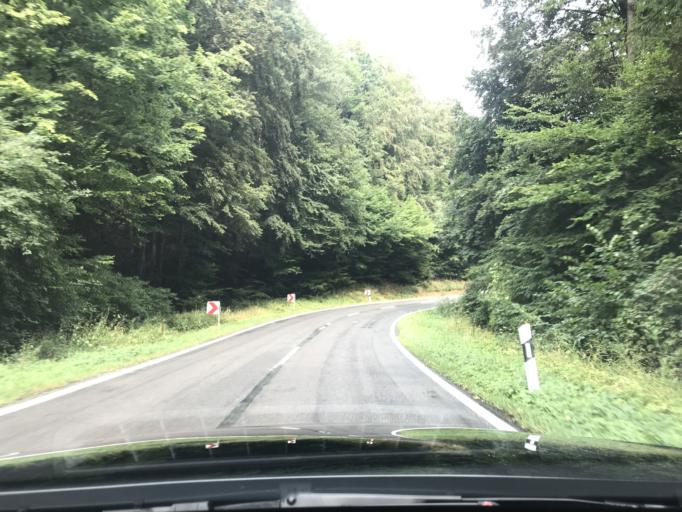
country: DE
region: Bavaria
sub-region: Regierungsbezirk Unterfranken
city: Eltmann
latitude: 49.9517
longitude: 10.6593
